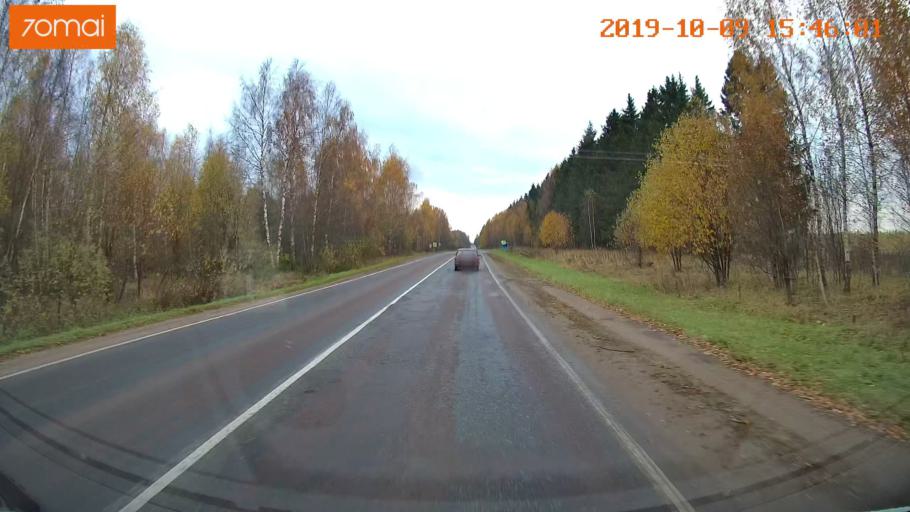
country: RU
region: Kostroma
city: Oktyabr'skiy
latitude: 57.8283
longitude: 41.0514
